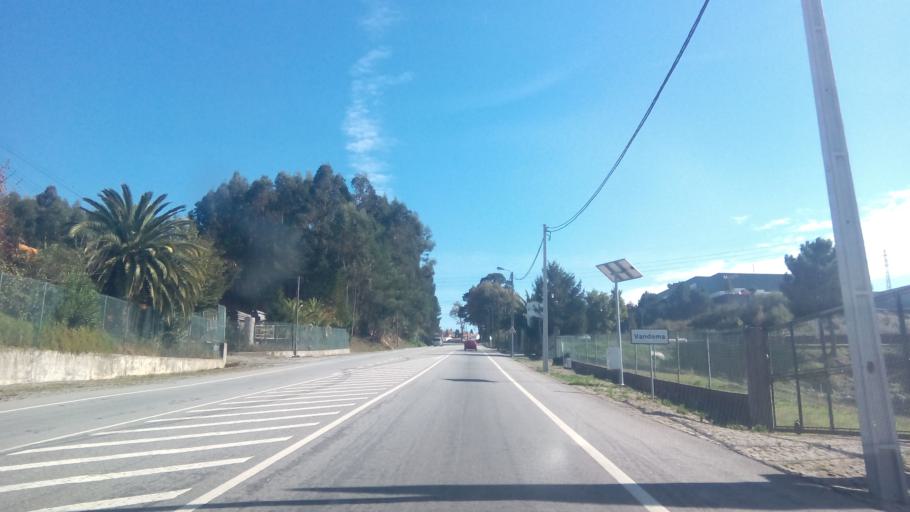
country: PT
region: Porto
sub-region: Paredes
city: Gandra
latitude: 41.1930
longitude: -8.4157
